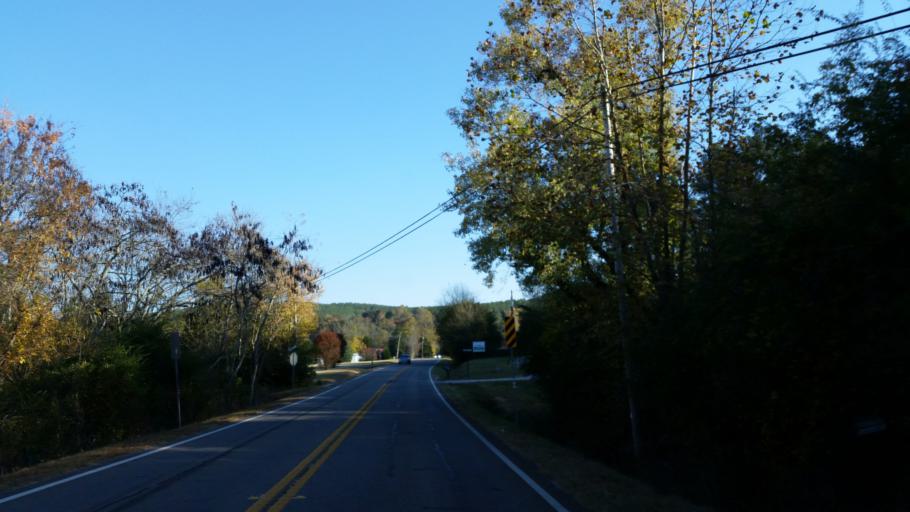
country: US
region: Georgia
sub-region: Pickens County
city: Jasper
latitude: 34.5116
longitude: -84.5149
